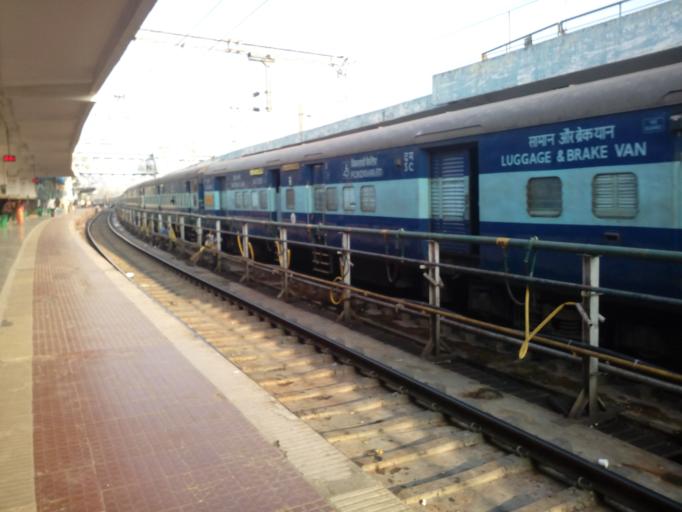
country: IN
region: Telangana
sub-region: Hyderabad
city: Malkajgiri
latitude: 17.4339
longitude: 78.5030
